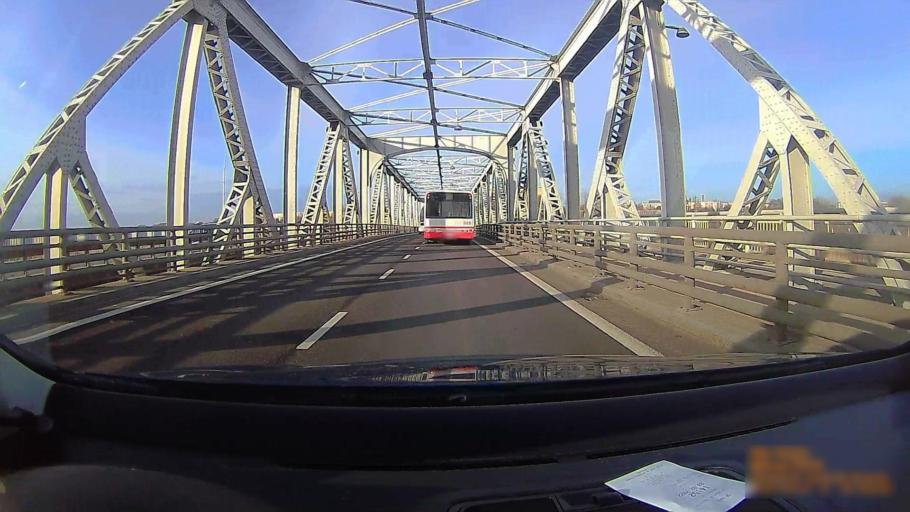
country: PL
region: Greater Poland Voivodeship
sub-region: Konin
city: Konin
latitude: 52.2199
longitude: 18.2524
